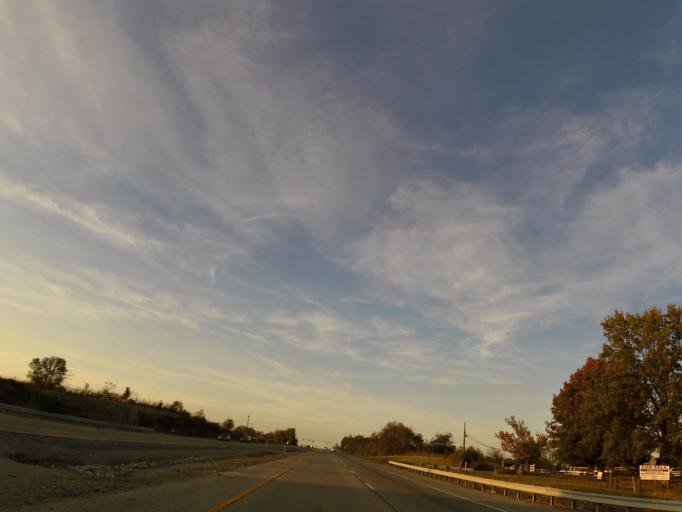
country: US
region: Kentucky
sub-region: Jessamine County
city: Nicholasville
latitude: 37.8477
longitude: -84.5859
